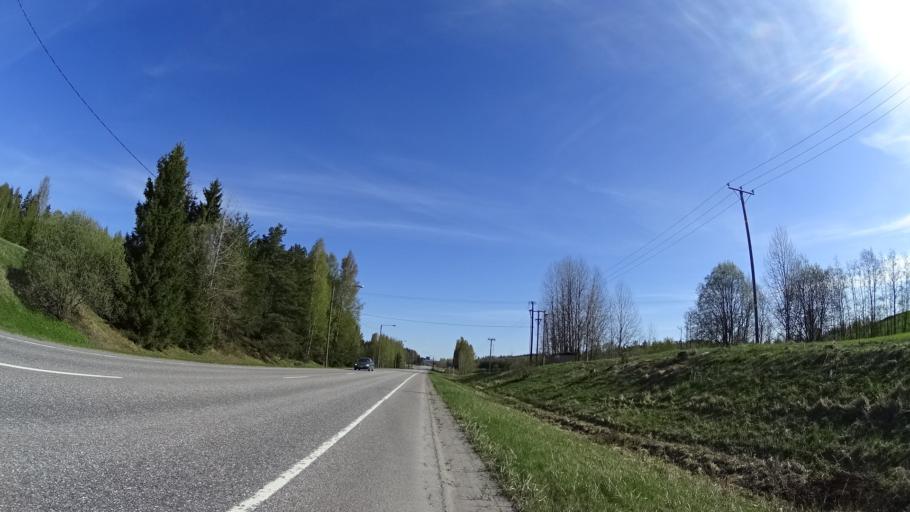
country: FI
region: Uusimaa
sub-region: Helsinki
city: Nurmijaervi
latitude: 60.3921
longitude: 24.8105
